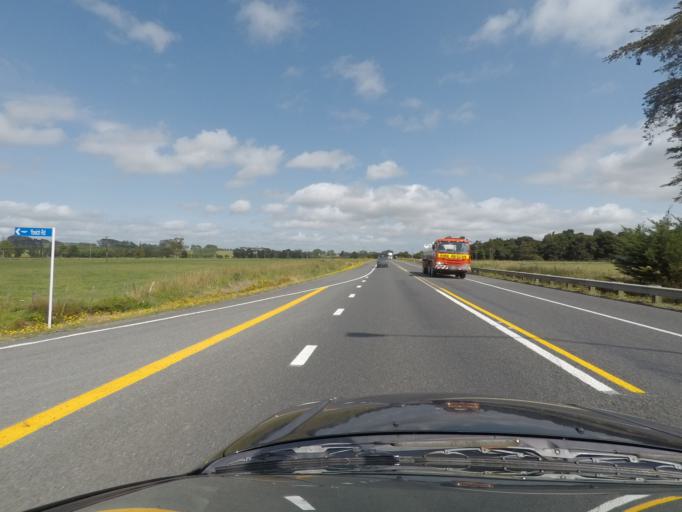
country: NZ
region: Northland
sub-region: Whangarei
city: Ruakaka
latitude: -35.8693
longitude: 174.4011
